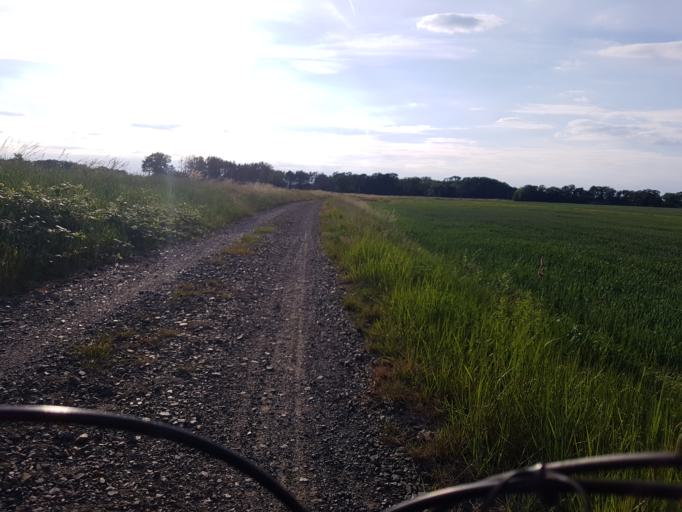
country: DE
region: Brandenburg
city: Elsterwerda
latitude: 51.4621
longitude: 13.4798
